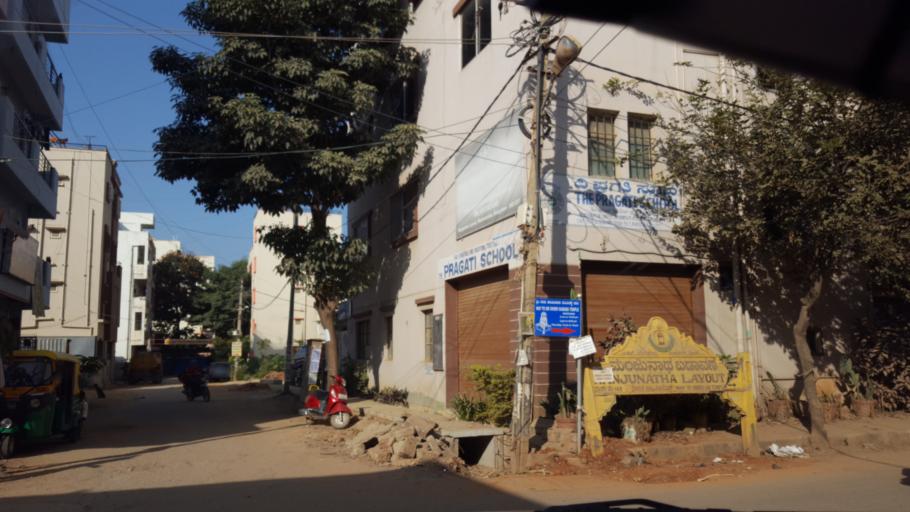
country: IN
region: Karnataka
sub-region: Bangalore Urban
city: Bangalore
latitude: 12.9502
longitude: 77.7093
